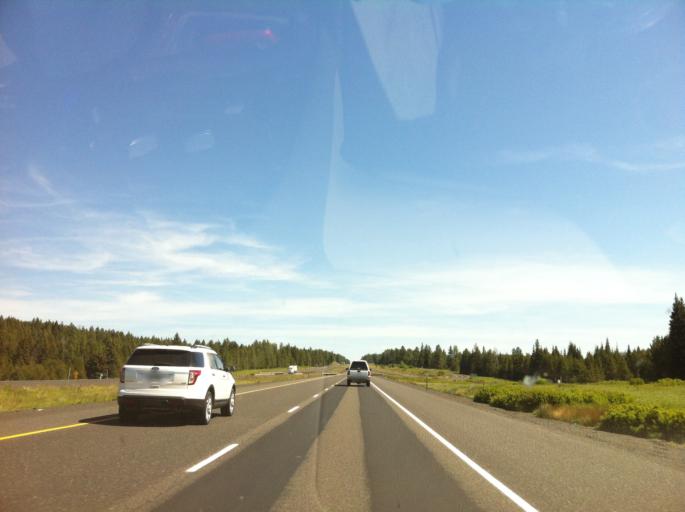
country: US
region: Oregon
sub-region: Umatilla County
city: Mission
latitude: 45.5097
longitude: -118.4291
